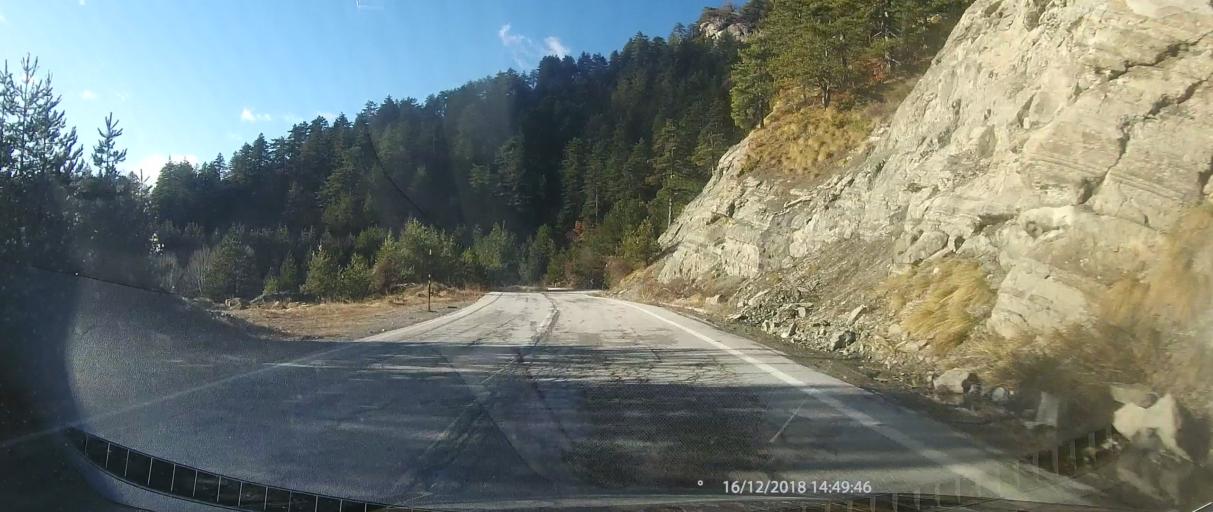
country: GR
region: West Macedonia
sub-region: Nomos Kastorias
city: Nestorio
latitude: 40.2094
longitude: 21.0850
